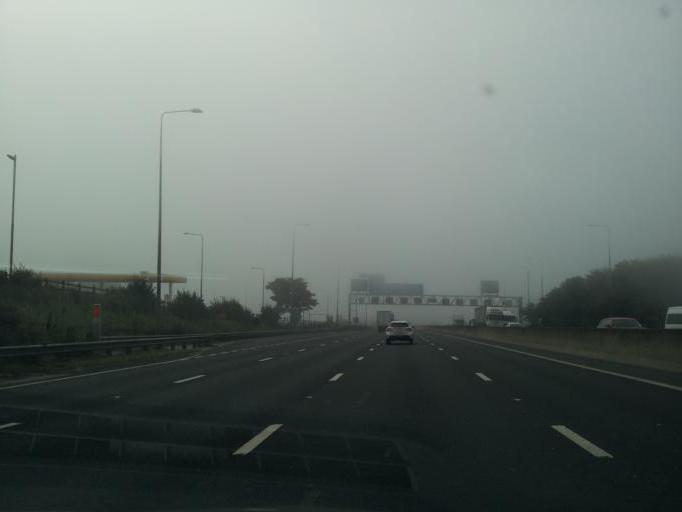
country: GB
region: England
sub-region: Kirklees
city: Cleckheaton
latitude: 53.7125
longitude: -1.7452
